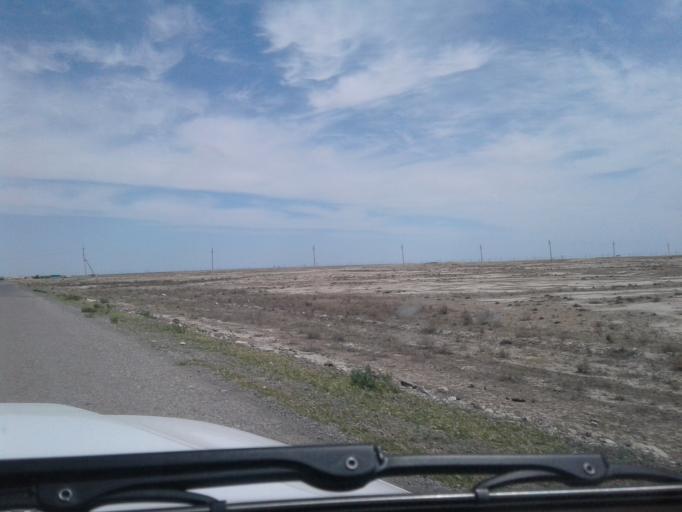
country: TM
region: Balkan
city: Gazanjyk
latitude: 39.2001
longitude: 55.7082
